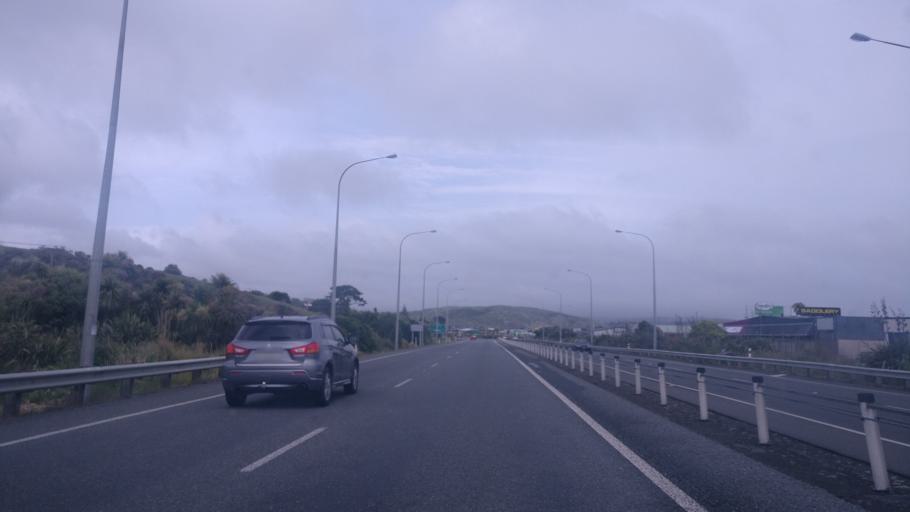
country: NZ
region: Wellington
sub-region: Porirua City
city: Porirua
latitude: -41.0792
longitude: 174.8720
